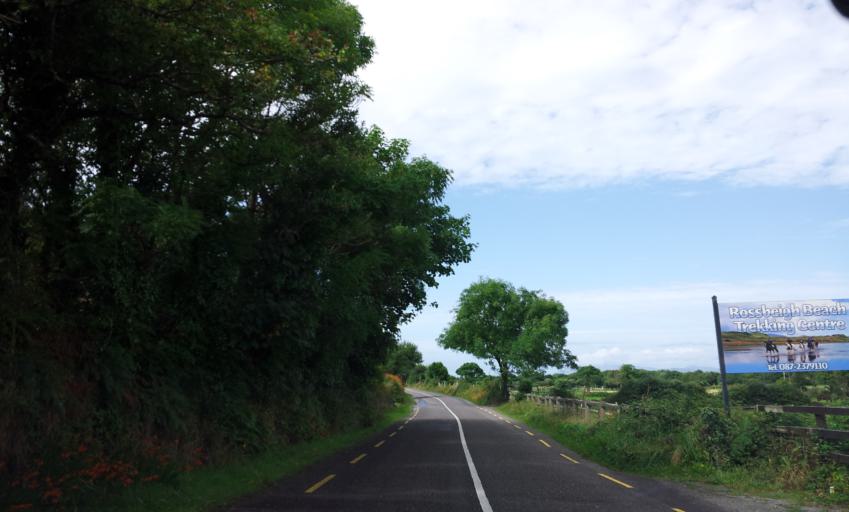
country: IE
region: Munster
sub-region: Ciarrai
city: Killorglin
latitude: 52.0559
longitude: -9.9562
